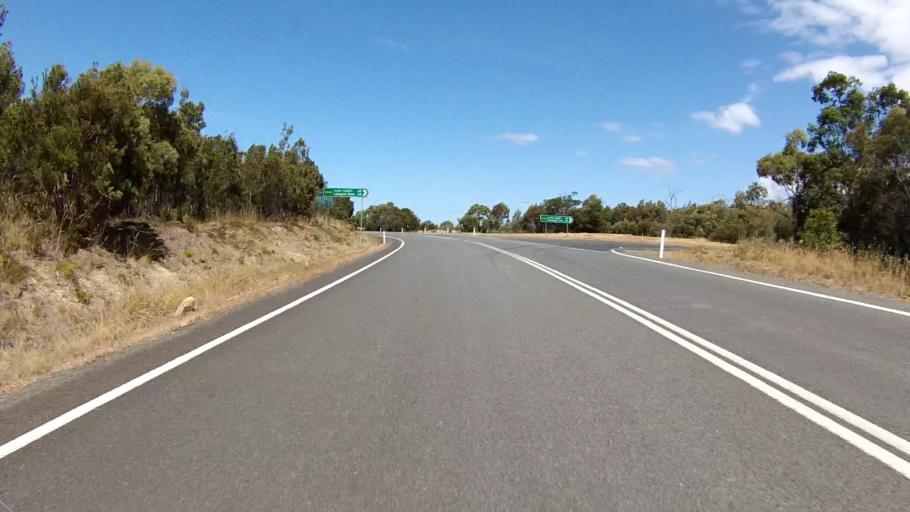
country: AU
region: Tasmania
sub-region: Break O'Day
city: St Helens
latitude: -42.0504
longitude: 148.0527
